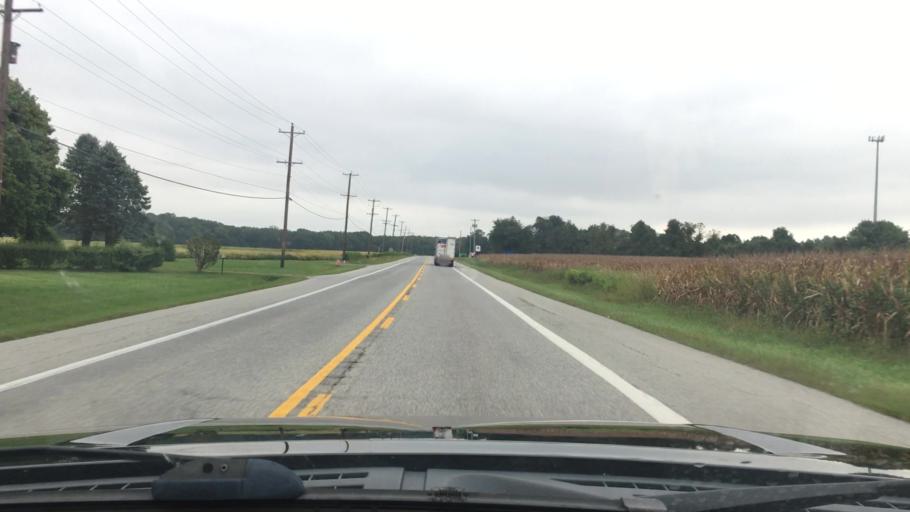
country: US
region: Maryland
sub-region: Cecil County
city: Elkton
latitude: 39.4904
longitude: -75.8446
